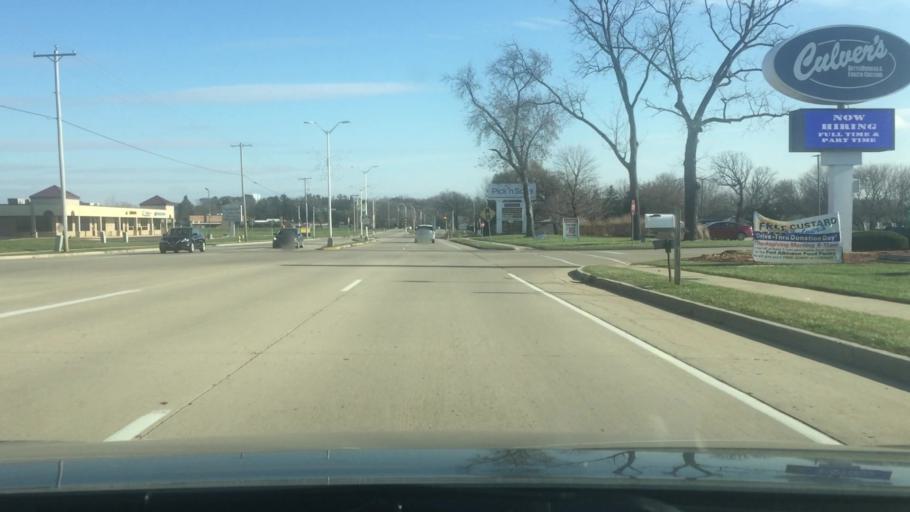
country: US
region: Wisconsin
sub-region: Jefferson County
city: Fort Atkinson
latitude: 42.9411
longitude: -88.8609
